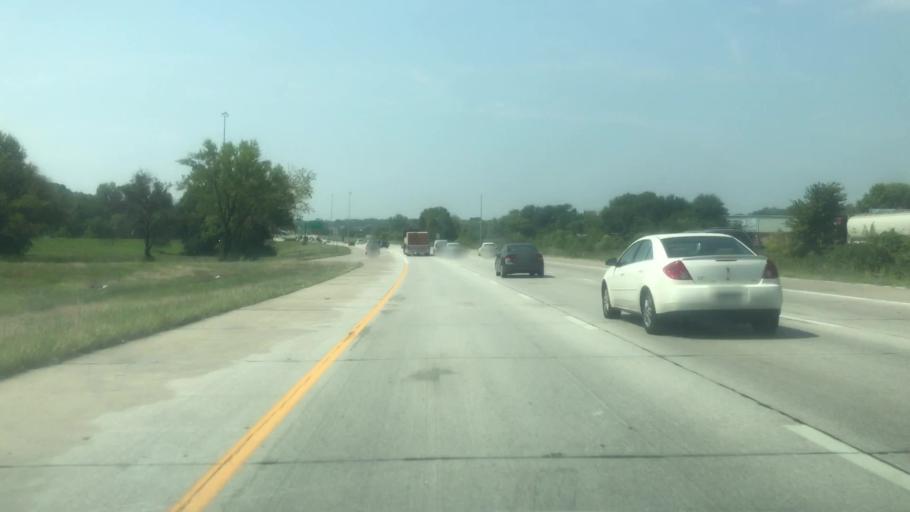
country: US
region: Kansas
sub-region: Johnson County
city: Merriam
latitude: 39.0401
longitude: -94.6771
